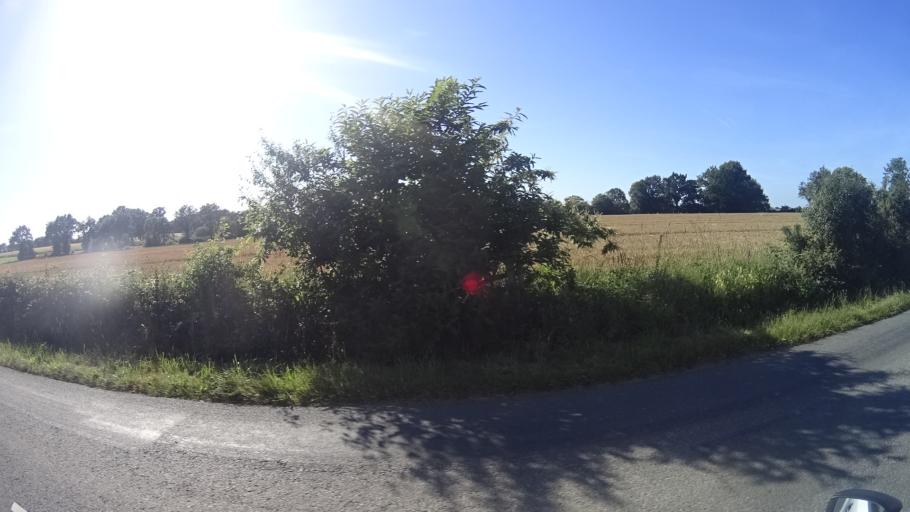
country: FR
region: Brittany
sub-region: Departement d'Ille-et-Vilaine
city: La Dominelais
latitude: 47.7515
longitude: -1.7026
